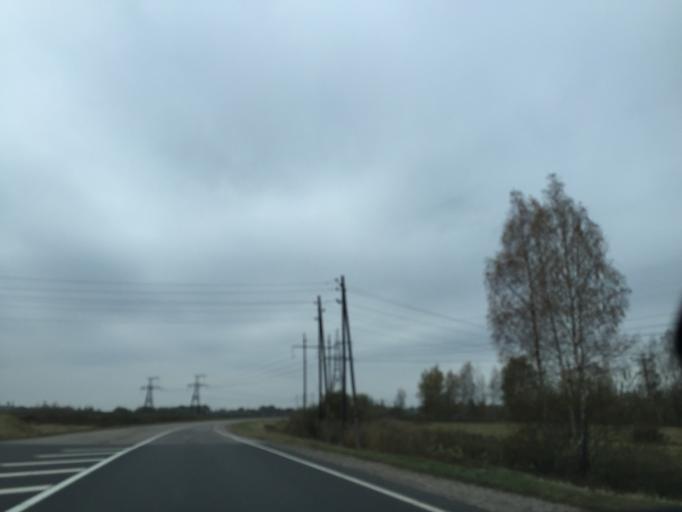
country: LV
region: Ozolnieku
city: Ozolnieki
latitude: 56.6569
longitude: 23.8073
